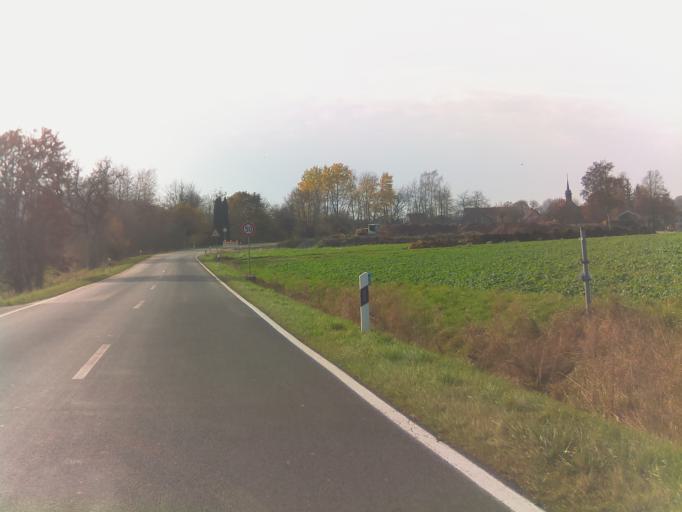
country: DE
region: Bavaria
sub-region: Regierungsbezirk Unterfranken
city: Schondra
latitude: 50.2503
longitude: 9.8574
